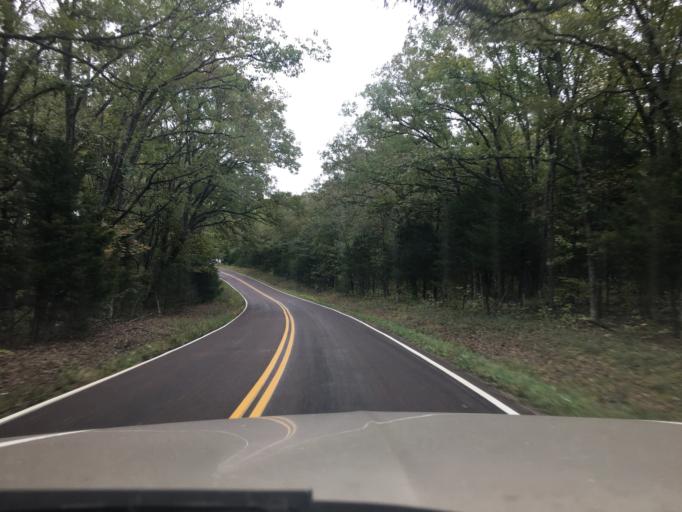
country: US
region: Missouri
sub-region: Crawford County
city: Cuba
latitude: 38.1949
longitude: -91.4615
